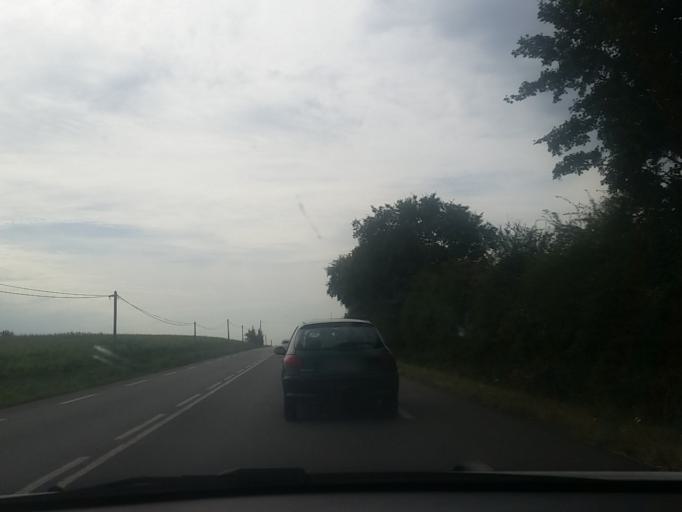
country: FR
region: Pays de la Loire
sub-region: Departement de la Vendee
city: Vendrennes
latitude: 46.7846
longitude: -1.1199
